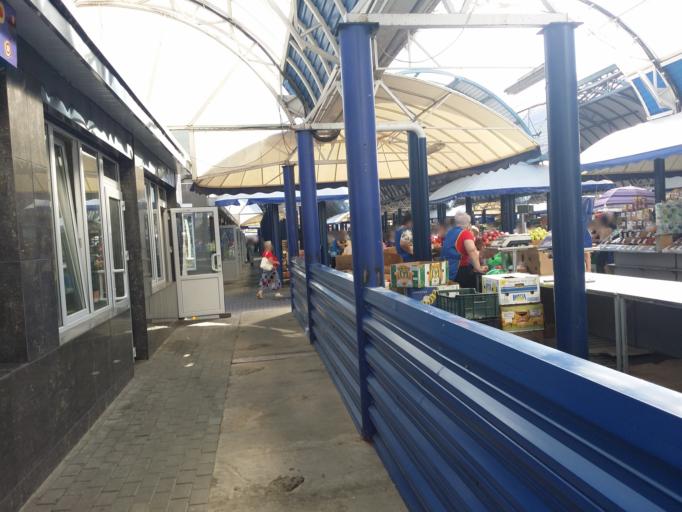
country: BY
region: Minsk
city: Minsk
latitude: 53.9200
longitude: 27.5797
